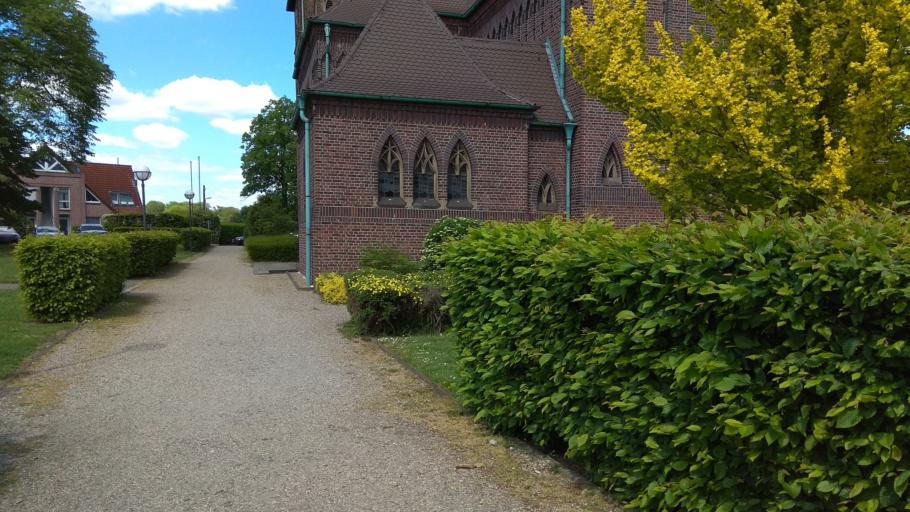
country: DE
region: North Rhine-Westphalia
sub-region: Regierungsbezirk Dusseldorf
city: Voerde
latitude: 51.5644
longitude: 6.7055
